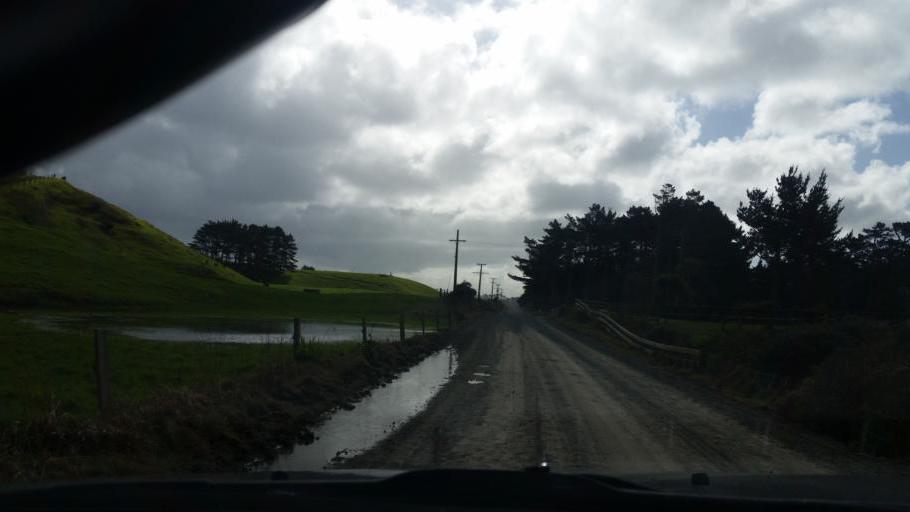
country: NZ
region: Northland
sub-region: Kaipara District
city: Dargaville
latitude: -36.0619
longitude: 173.8769
